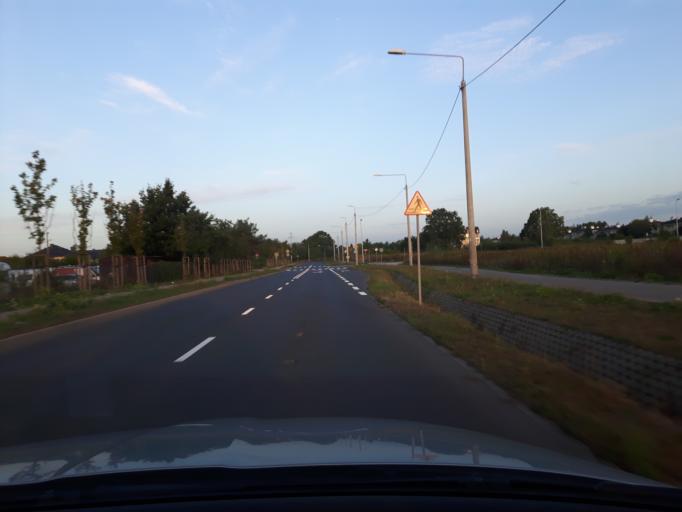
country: PL
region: Masovian Voivodeship
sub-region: Warszawa
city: Wawer
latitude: 52.1865
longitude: 21.1504
